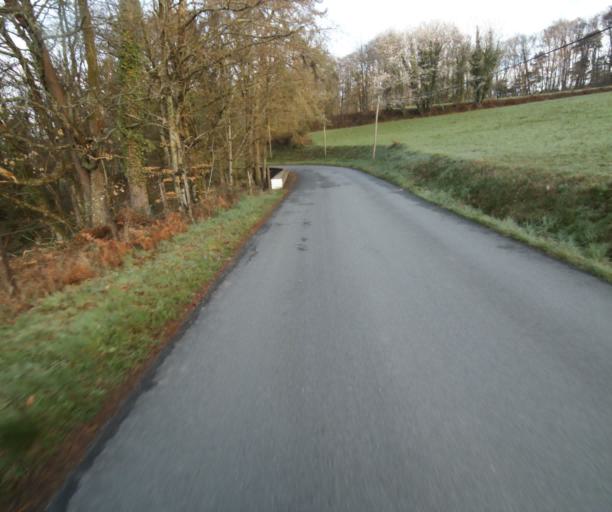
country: FR
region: Limousin
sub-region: Departement de la Correze
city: Correze
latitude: 45.3055
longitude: 1.8532
